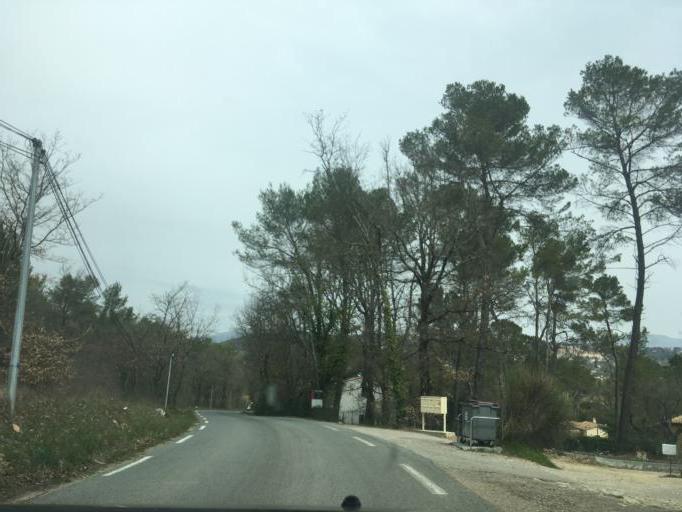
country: FR
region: Provence-Alpes-Cote d'Azur
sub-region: Departement du Var
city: Callian
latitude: 43.6035
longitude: 6.7420
